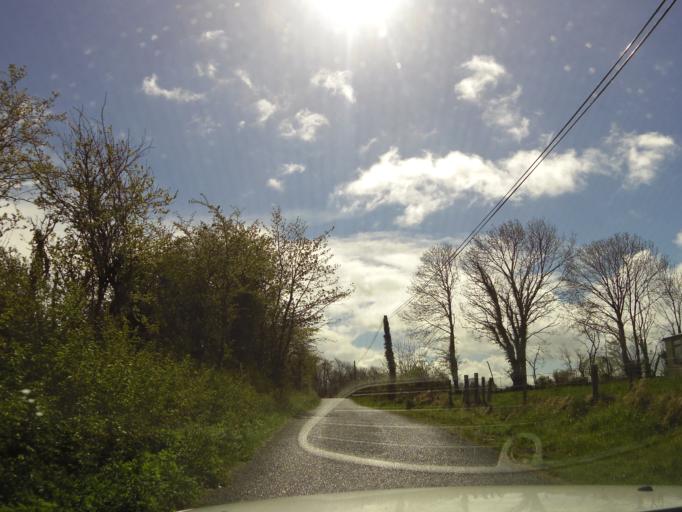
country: IE
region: Connaught
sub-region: Maigh Eo
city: Kiltamagh
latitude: 53.7954
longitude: -8.9655
